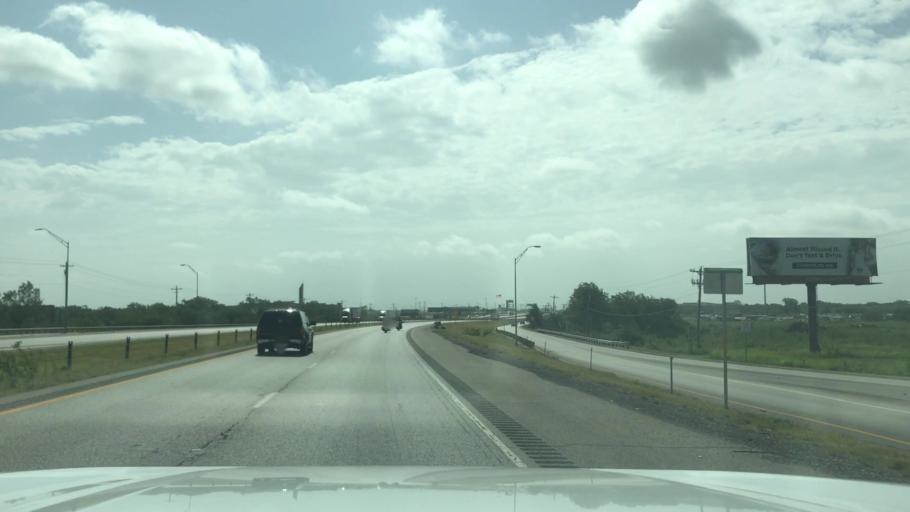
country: US
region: Texas
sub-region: Taylor County
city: Abilene
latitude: 32.4893
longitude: -99.7193
